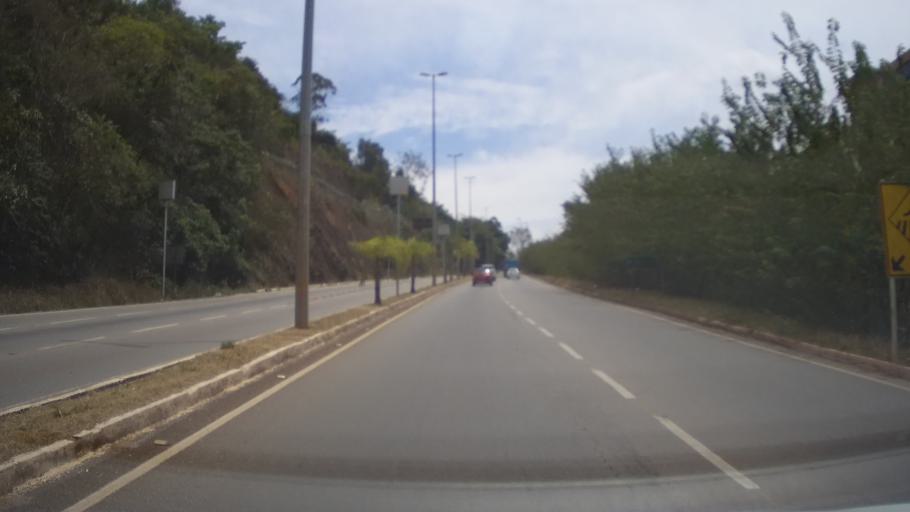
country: BR
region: Minas Gerais
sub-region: Nova Lima
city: Nova Lima
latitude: -19.9955
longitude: -43.8582
